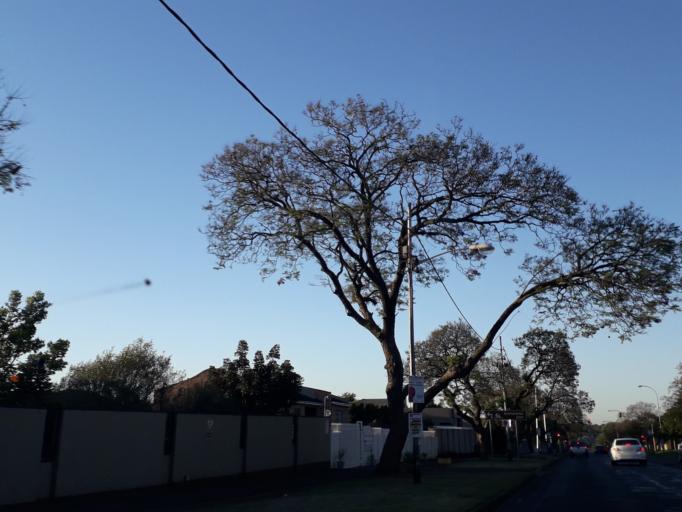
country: ZA
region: Gauteng
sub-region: City of Johannesburg Metropolitan Municipality
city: Johannesburg
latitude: -26.1531
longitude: 28.0104
